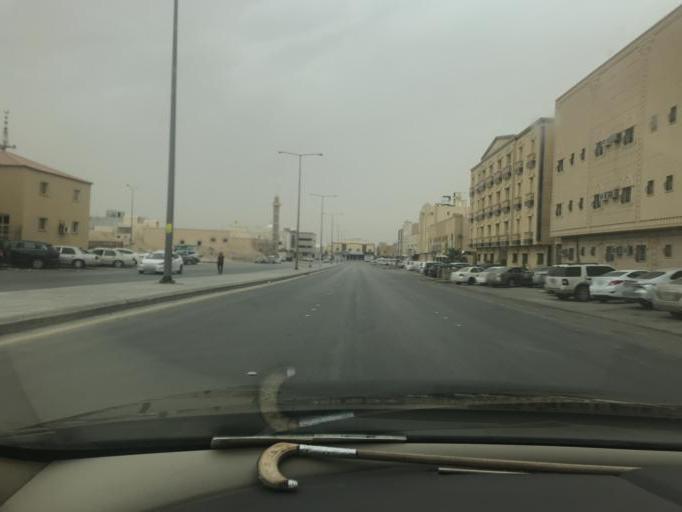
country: SA
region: Ar Riyad
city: Riyadh
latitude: 24.7883
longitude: 46.6931
